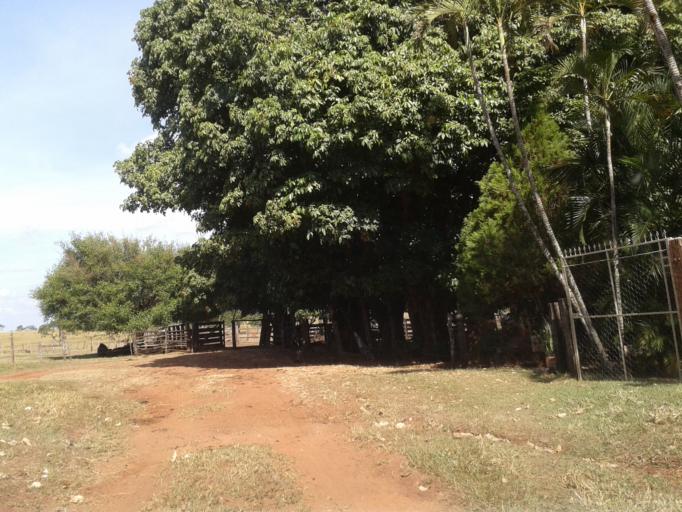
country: BR
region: Minas Gerais
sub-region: Campina Verde
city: Campina Verde
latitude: -19.5168
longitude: -49.5636
